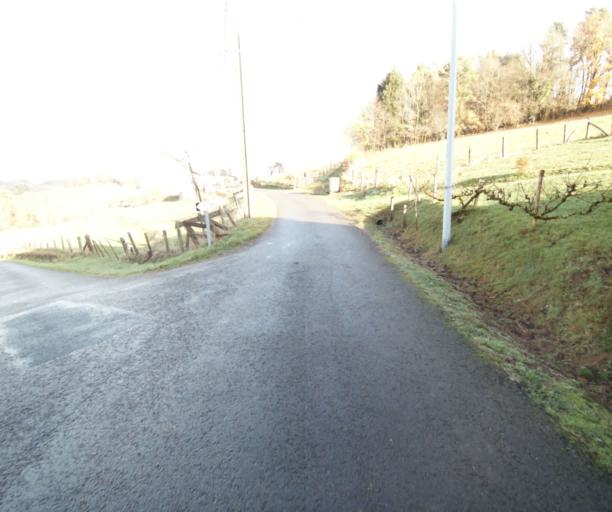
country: FR
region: Limousin
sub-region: Departement de la Correze
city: Saint-Mexant
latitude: 45.2377
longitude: 1.6511
